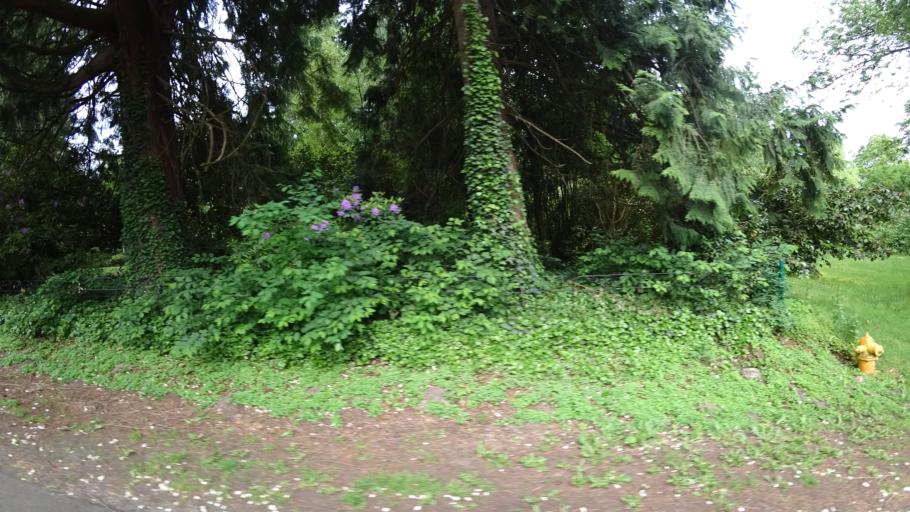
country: US
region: Oregon
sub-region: Washington County
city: Garden Home-Whitford
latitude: 45.4707
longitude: -122.7476
